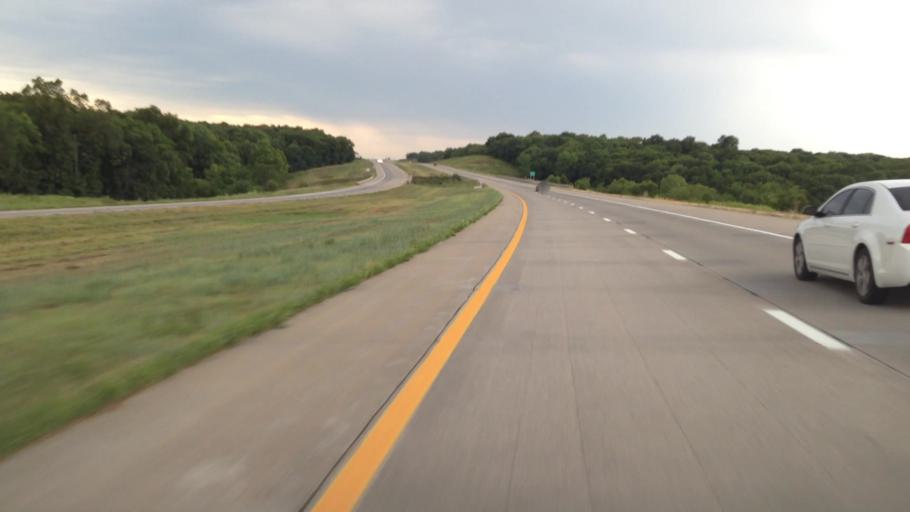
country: US
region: Kansas
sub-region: Osage County
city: Lyndon
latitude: 38.4858
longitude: -95.4893
